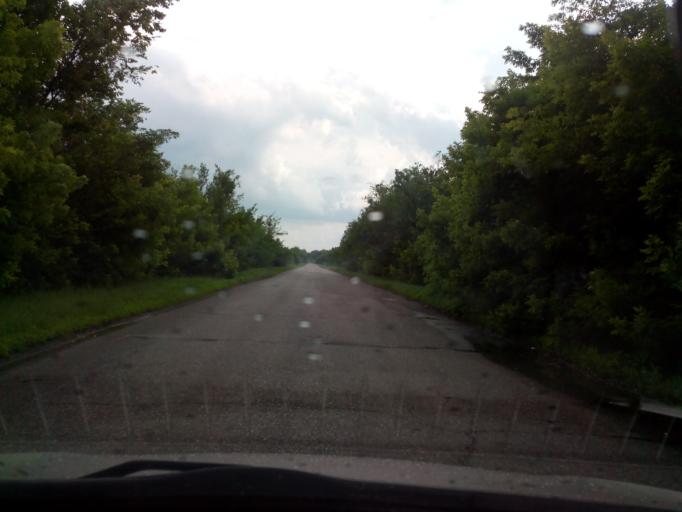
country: RU
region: Volgograd
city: Mikhaylovka
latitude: 49.9130
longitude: 42.9799
